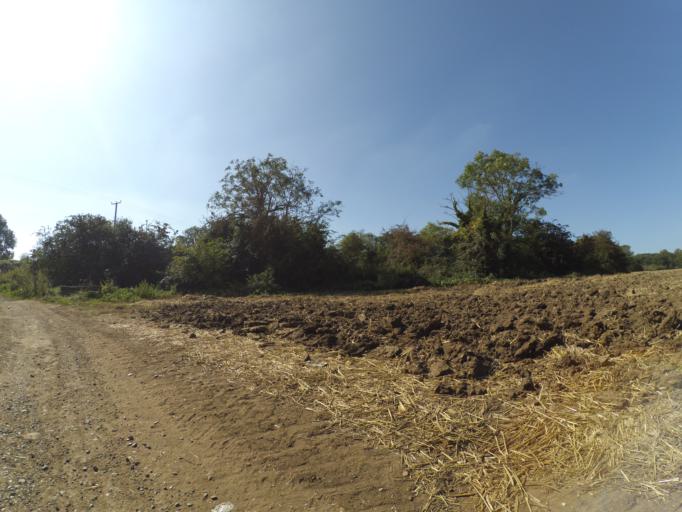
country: GB
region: England
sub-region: Warwickshire
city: Rugby
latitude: 52.4088
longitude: -1.2647
